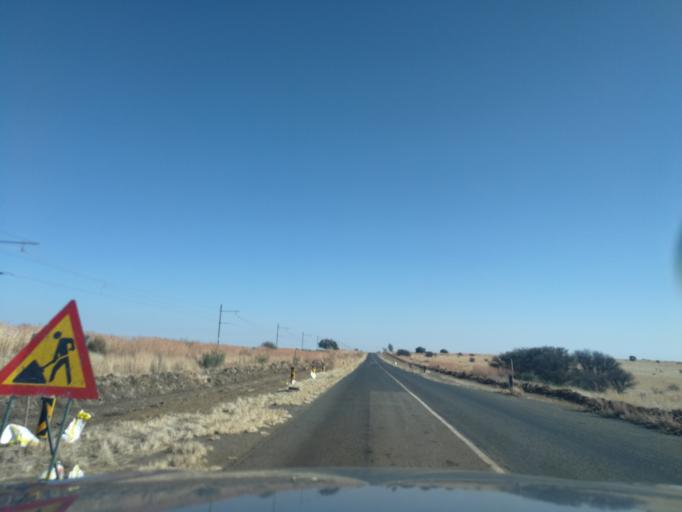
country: ZA
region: Orange Free State
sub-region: Fezile Dabi District Municipality
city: Kroonstad
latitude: -27.8992
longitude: 27.5067
